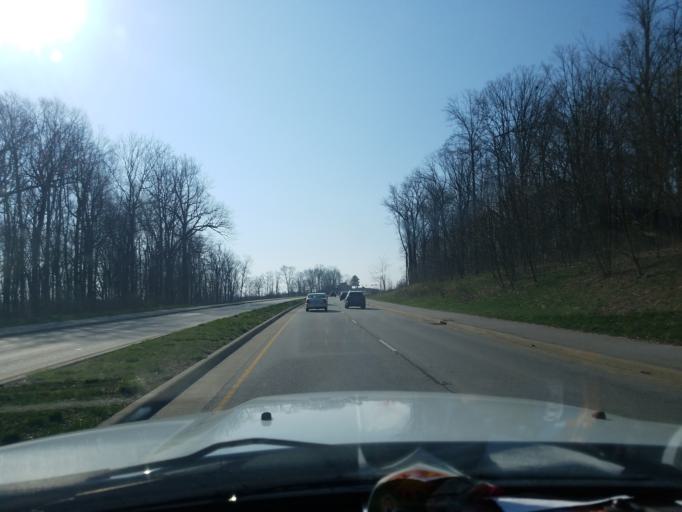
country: US
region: Indiana
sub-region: Monroe County
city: Bloomington
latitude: 39.1824
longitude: -86.5105
